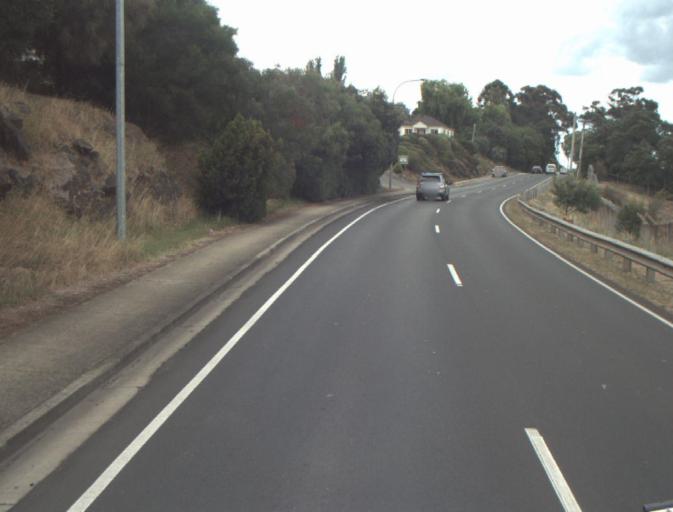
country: AU
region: Tasmania
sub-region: Launceston
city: Launceston
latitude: -41.4235
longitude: 147.1118
